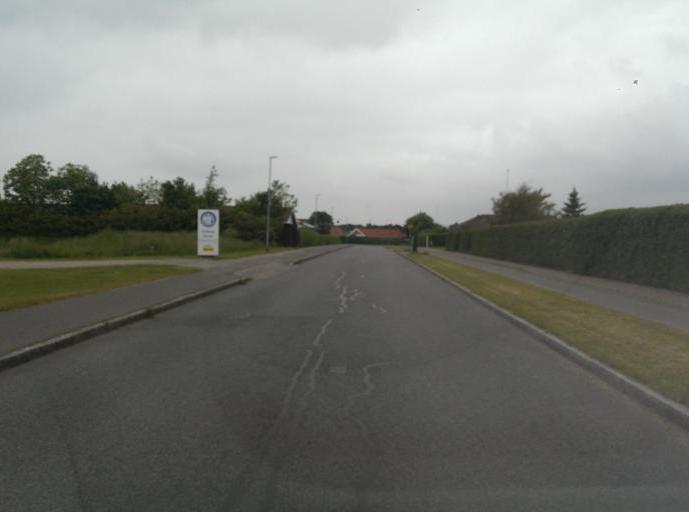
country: DK
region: South Denmark
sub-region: Fano Kommune
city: Nordby
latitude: 55.5310
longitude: 8.3669
